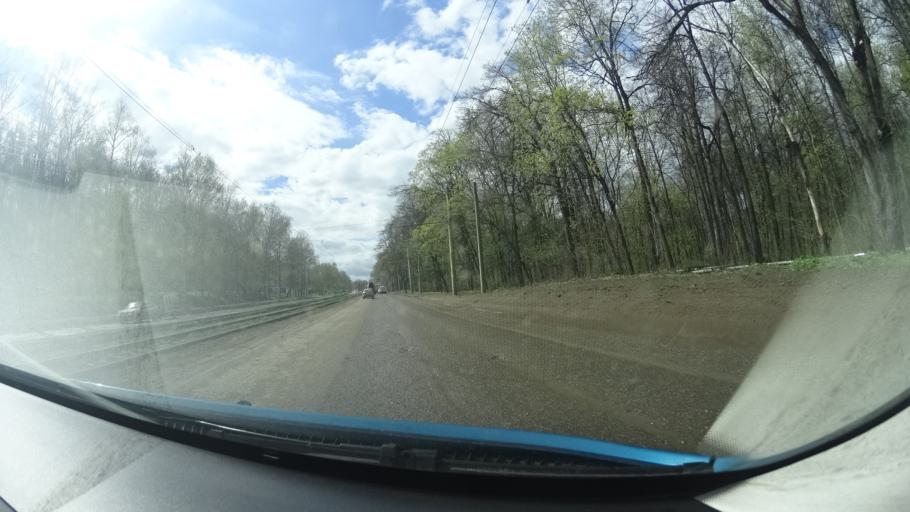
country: RU
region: Bashkortostan
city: Ufa
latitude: 54.7965
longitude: 56.0470
